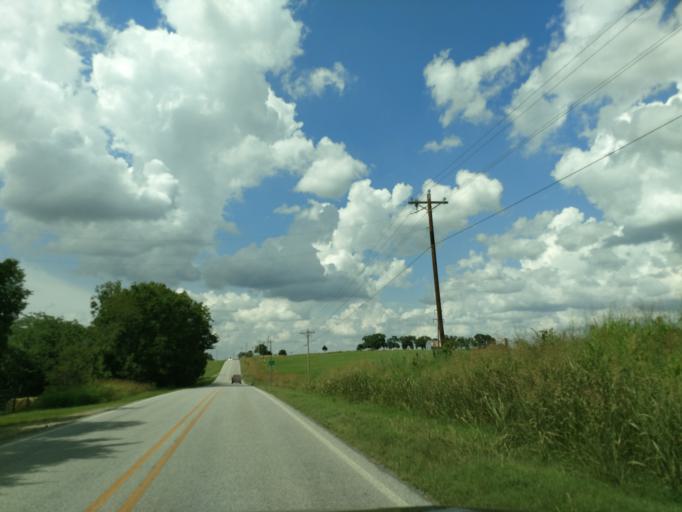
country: US
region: Arkansas
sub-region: Carroll County
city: Berryville
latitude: 36.4650
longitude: -93.5558
